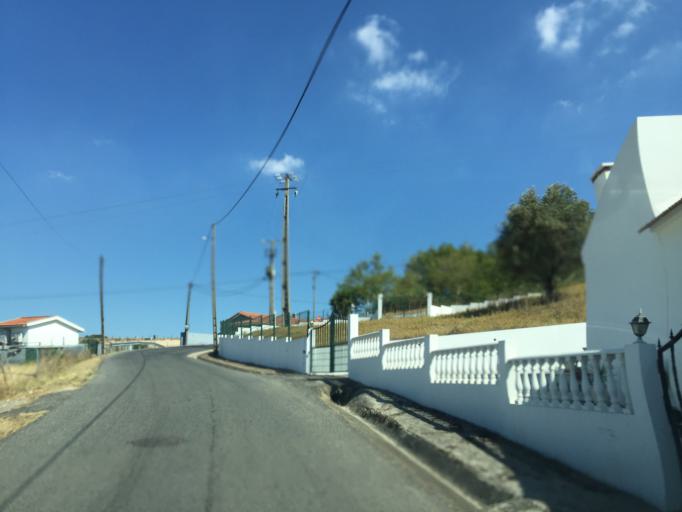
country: PT
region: Lisbon
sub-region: Azambuja
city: Aveiras de Cima
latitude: 39.1642
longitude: -8.8744
